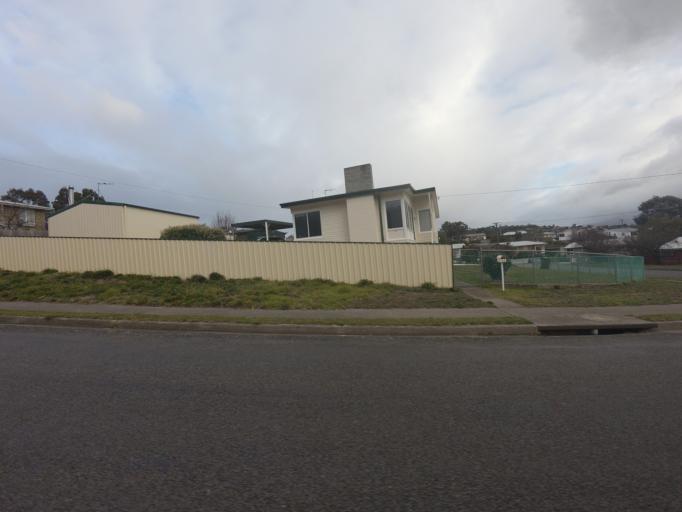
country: AU
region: Tasmania
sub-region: Clarence
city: Warrane
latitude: -42.8567
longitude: 147.3994
